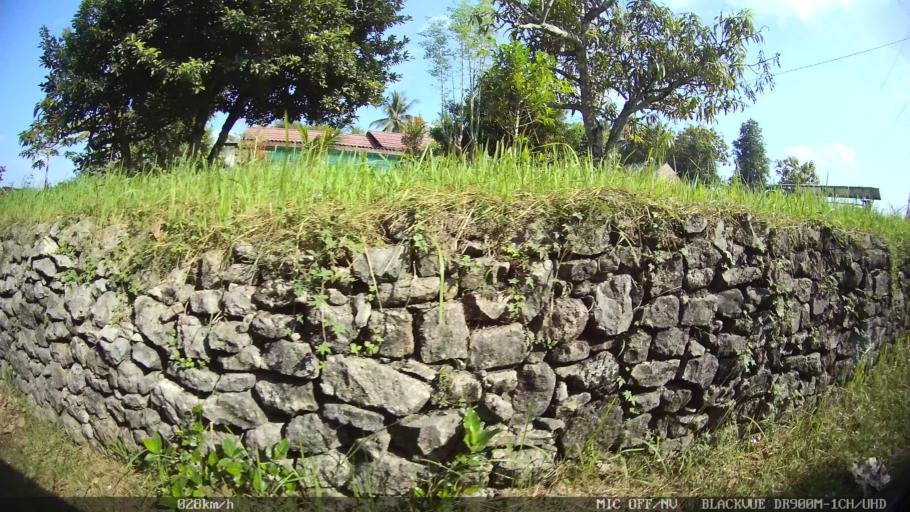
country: ID
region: Daerah Istimewa Yogyakarta
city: Kasihan
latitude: -7.8156
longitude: 110.2986
